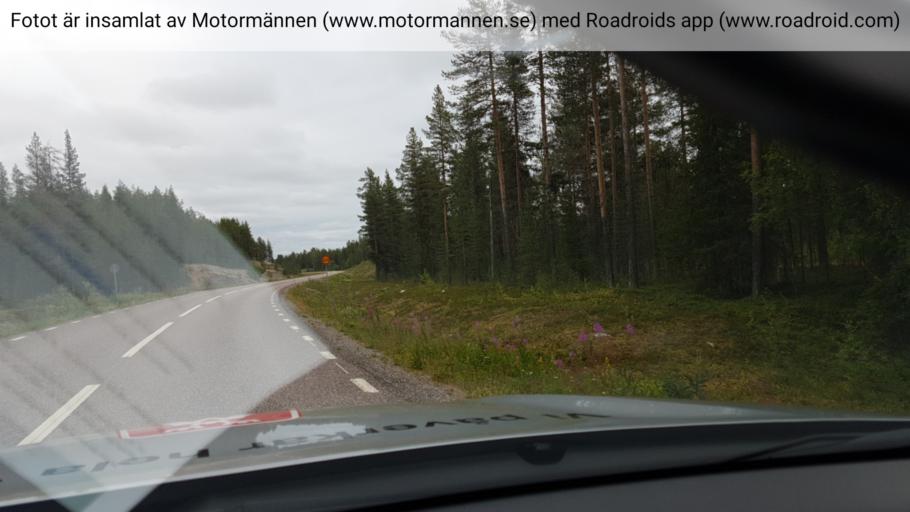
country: SE
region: Norrbotten
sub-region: Gallivare Kommun
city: Gaellivare
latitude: 67.0774
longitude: 21.3441
